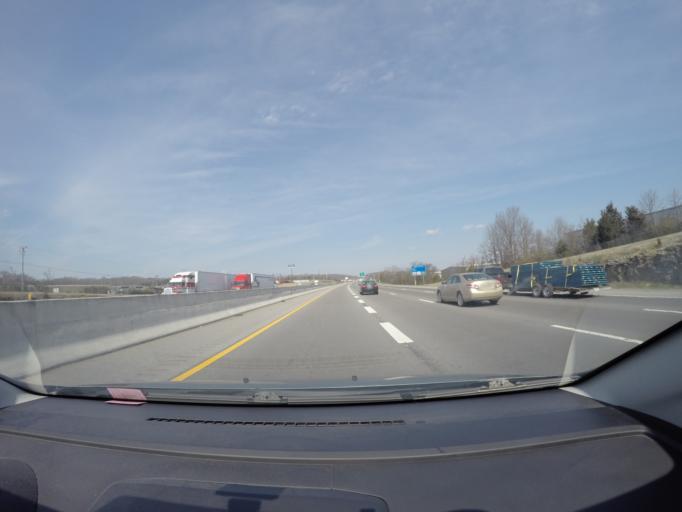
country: US
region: Tennessee
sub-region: Rutherford County
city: La Vergne
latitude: 36.0011
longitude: -86.6055
